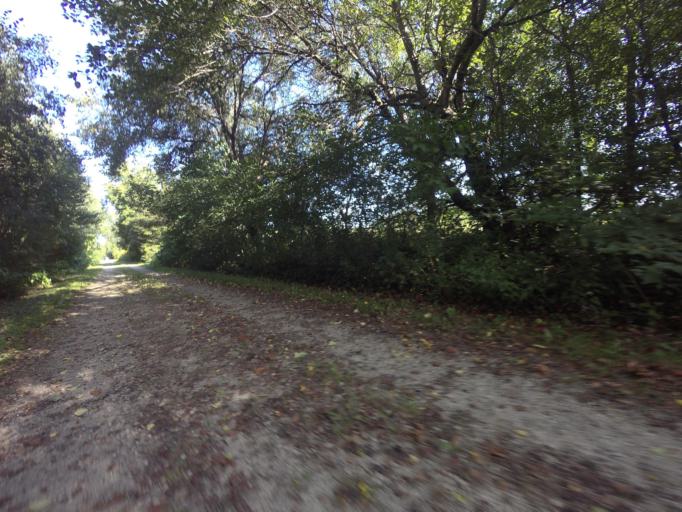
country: CA
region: Ontario
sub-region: Wellington County
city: Guelph
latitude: 43.6624
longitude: -80.4319
